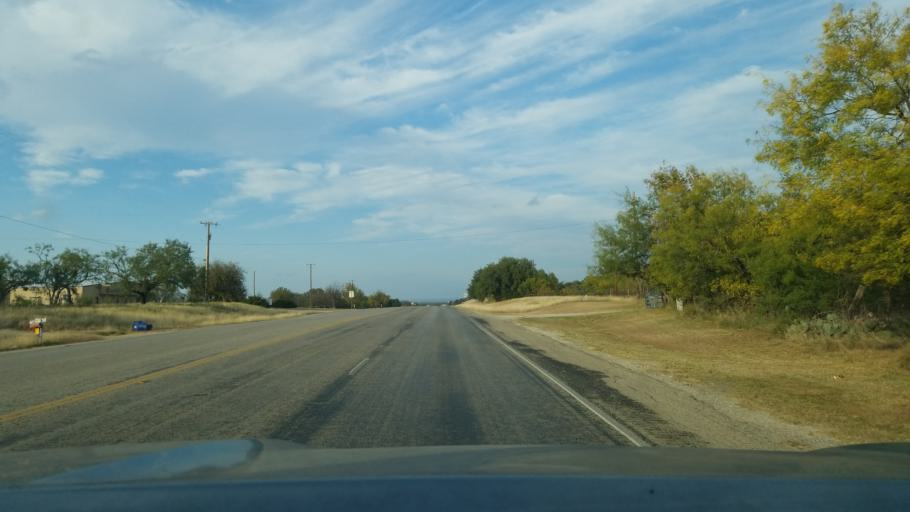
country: US
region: Texas
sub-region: Brown County
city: Early
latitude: 31.7704
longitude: -98.9529
